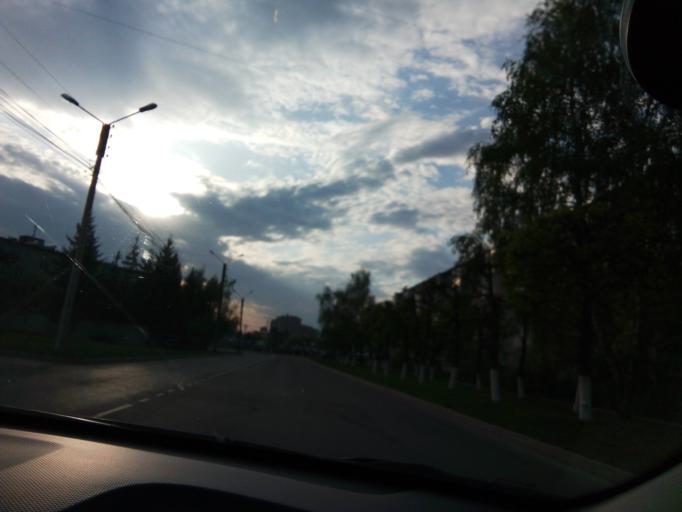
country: RU
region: Chuvashia
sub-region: Cheboksarskiy Rayon
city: Cheboksary
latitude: 56.1224
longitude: 47.2770
